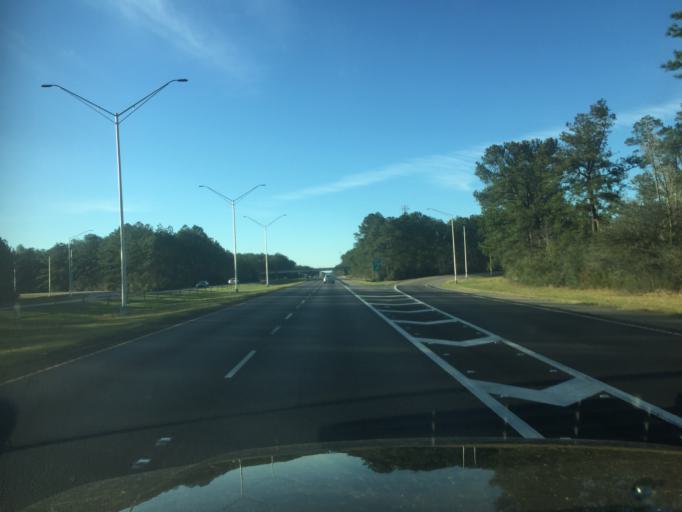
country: US
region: Louisiana
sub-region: Saint Tammany Parish
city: Lacombe
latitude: 30.3503
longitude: -89.9164
